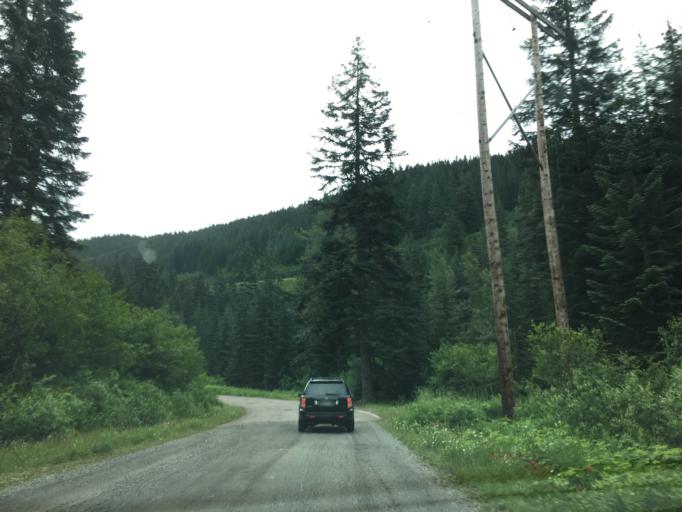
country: US
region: Washington
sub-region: Chelan County
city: Leavenworth
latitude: 47.7496
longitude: -121.1152
